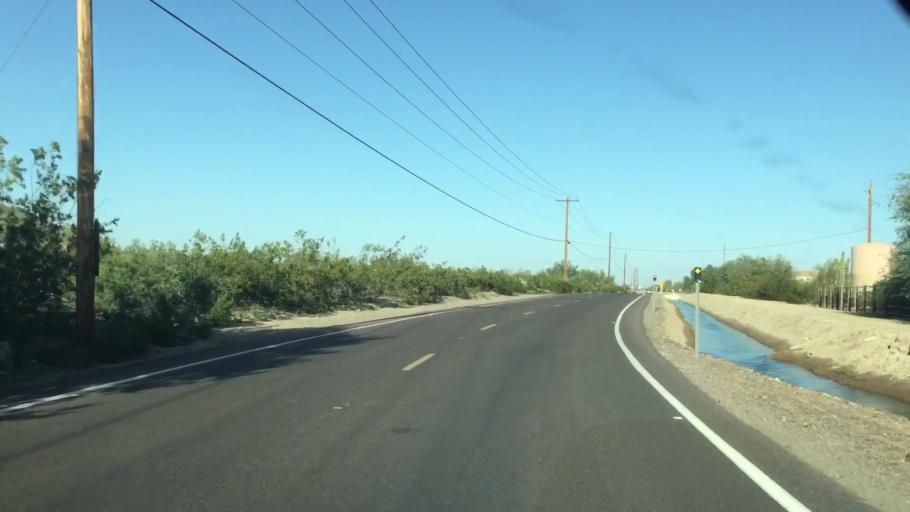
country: US
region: Arizona
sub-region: Maricopa County
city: Laveen
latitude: 33.3465
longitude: -112.1381
